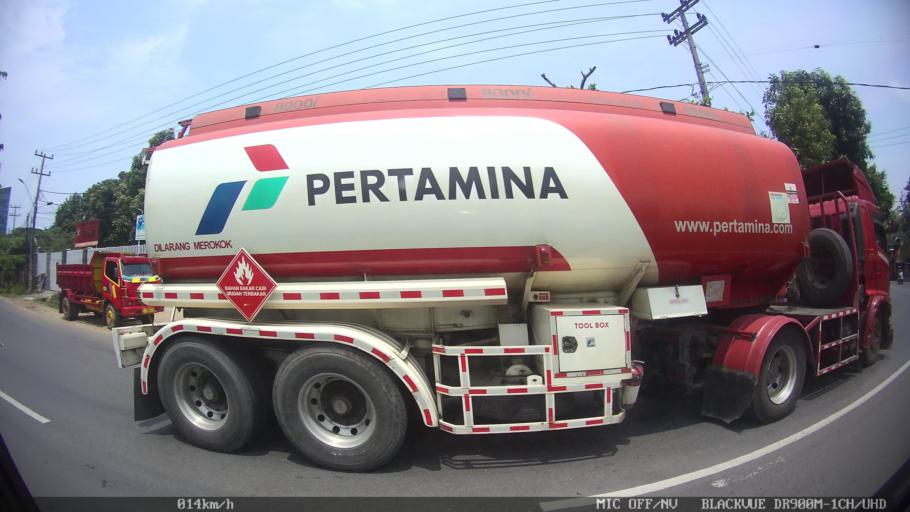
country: ID
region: Lampung
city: Bandarlampung
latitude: -5.4369
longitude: 105.2888
